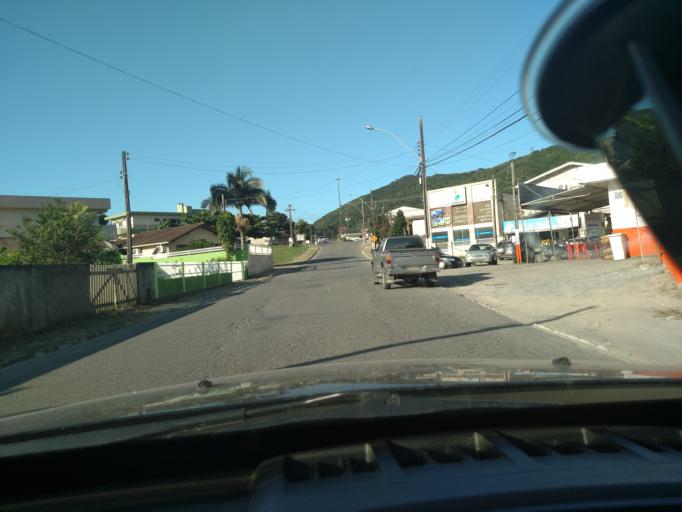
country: BR
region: Santa Catarina
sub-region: Porto Belo
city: Porto Belo
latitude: -27.1739
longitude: -48.5231
